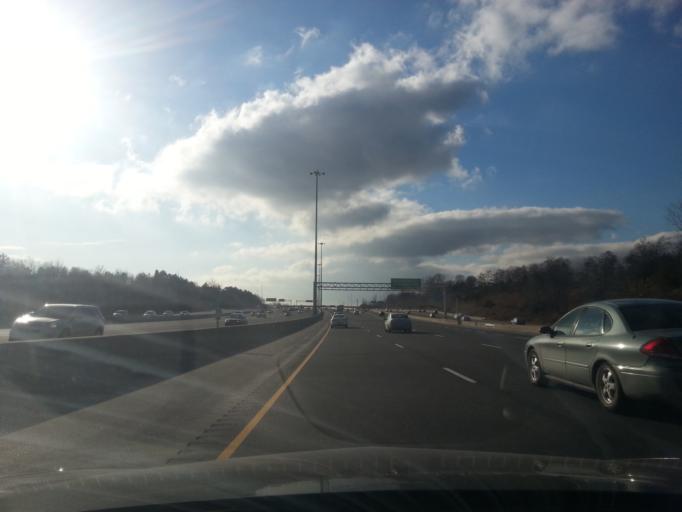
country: CA
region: Ontario
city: Pickering
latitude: 43.8039
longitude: -79.1356
